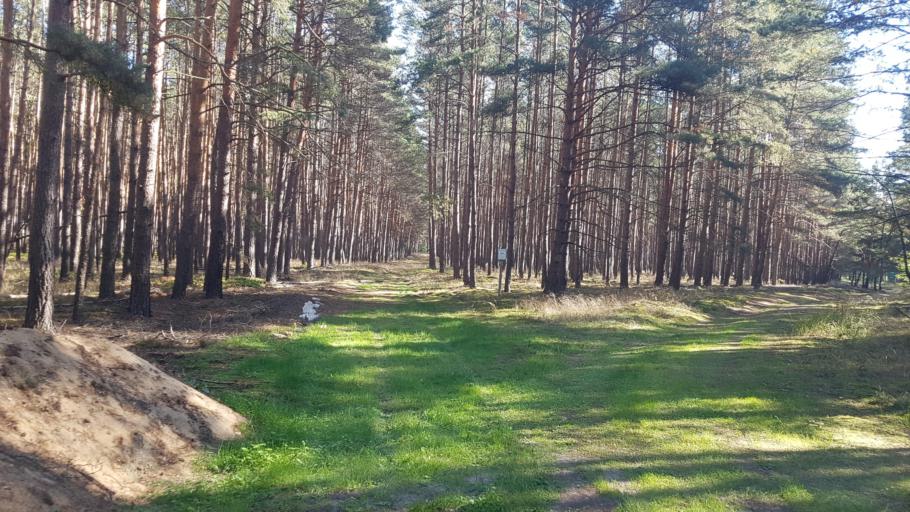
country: DE
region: Brandenburg
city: Hohenbucko
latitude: 51.8222
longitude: 13.5073
